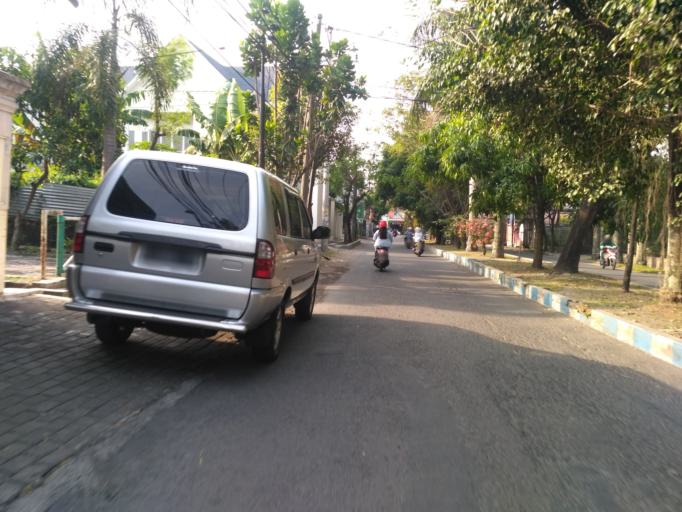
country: ID
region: East Java
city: Malang
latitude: -7.9401
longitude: 112.6300
